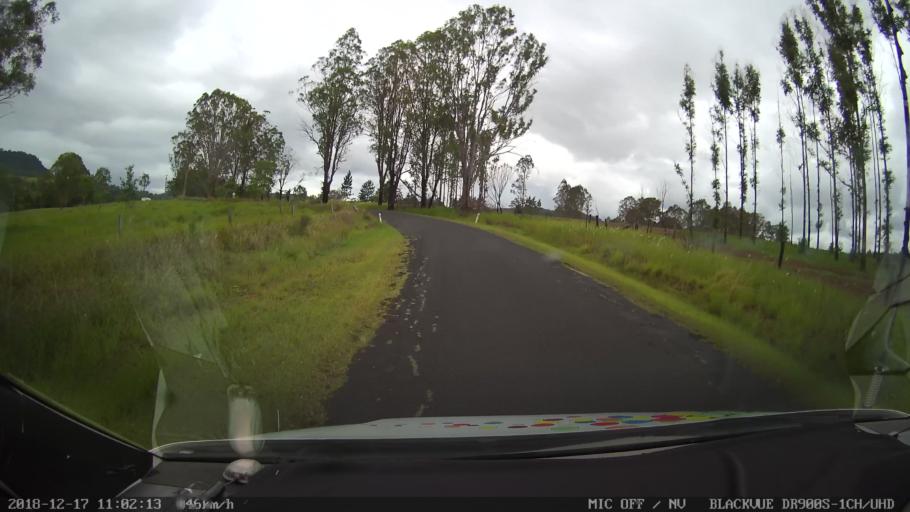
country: AU
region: New South Wales
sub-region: Richmond Valley
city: Casino
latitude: -28.8133
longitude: 152.6309
